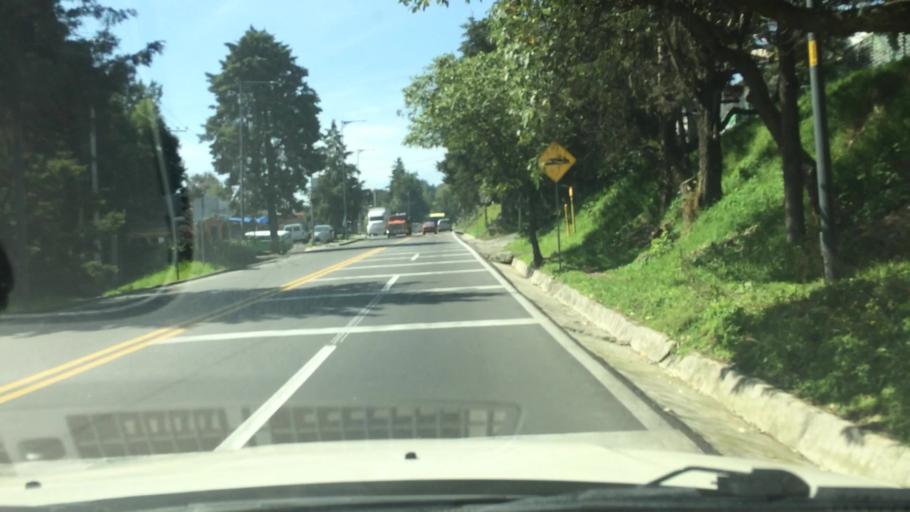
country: MX
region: Mexico City
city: Tlalpan
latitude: 19.2399
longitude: -99.1608
